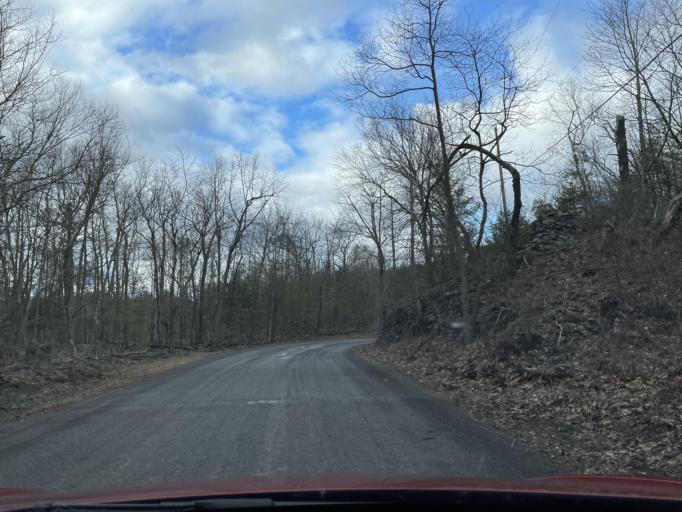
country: US
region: New York
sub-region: Ulster County
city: Zena
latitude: 42.0793
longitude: -74.0586
